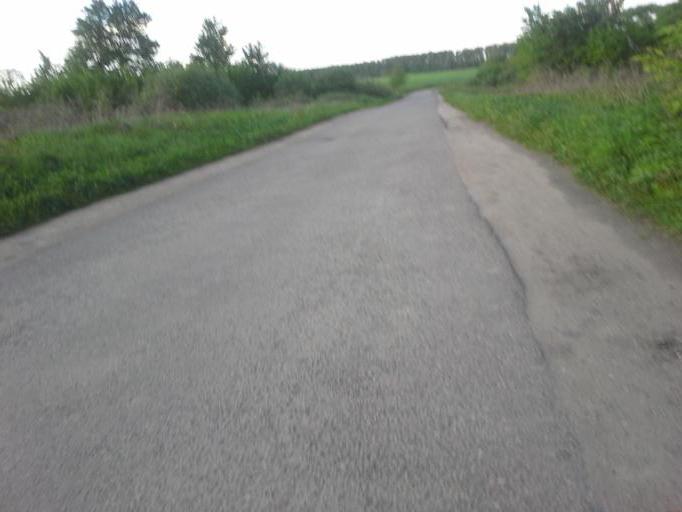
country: RU
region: Moskovskaya
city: Zhavoronki
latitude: 55.6621
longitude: 37.1358
